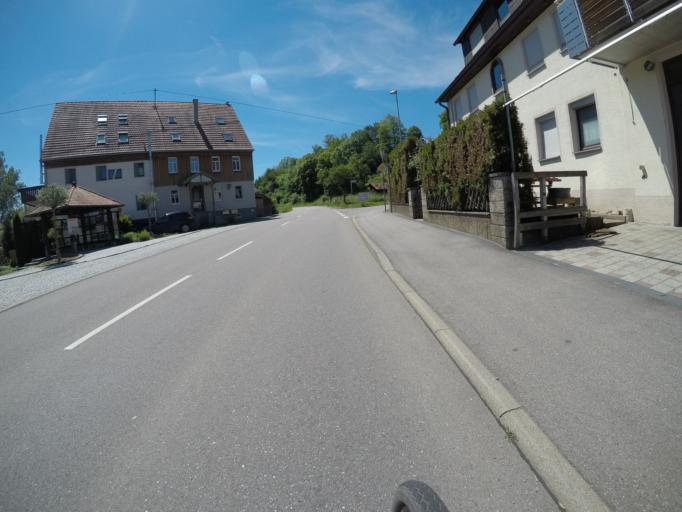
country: DE
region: Baden-Wuerttemberg
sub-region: Karlsruhe Region
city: Heimsheim
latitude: 48.7886
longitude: 8.8339
